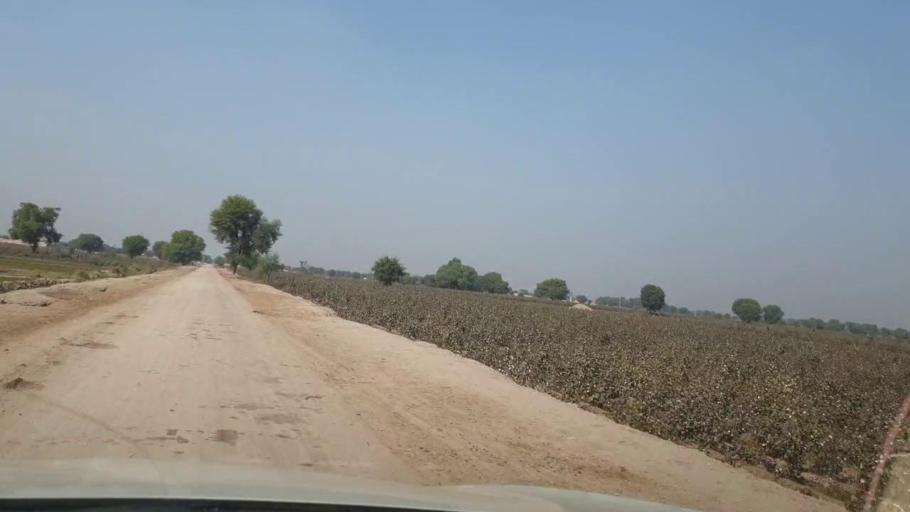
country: PK
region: Sindh
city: Bhan
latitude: 26.5397
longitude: 67.7432
